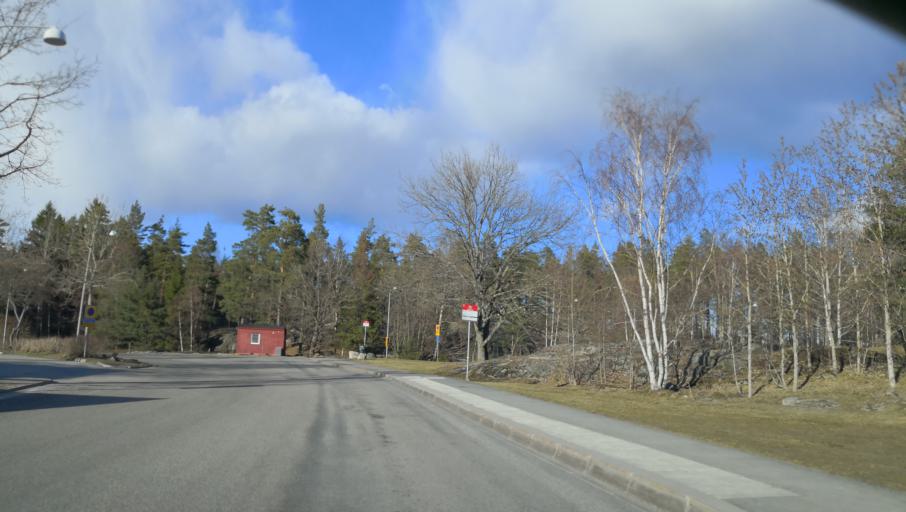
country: SE
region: Stockholm
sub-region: Varmdo Kommun
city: Gustavsberg
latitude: 59.3385
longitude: 18.3941
